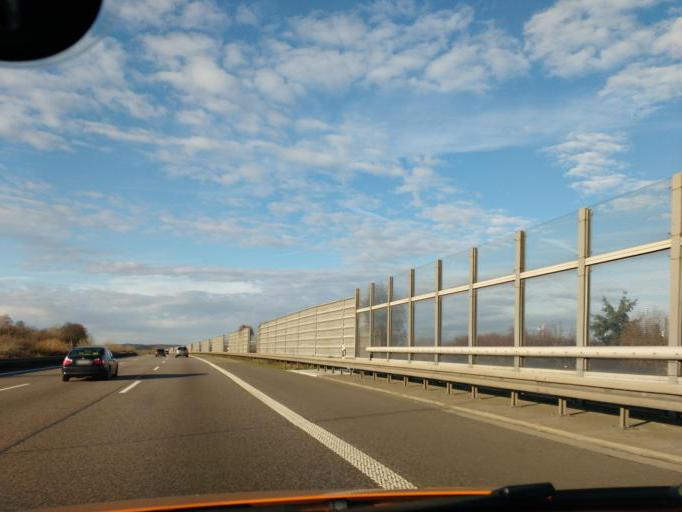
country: DE
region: Saxony-Anhalt
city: Wefensleben
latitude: 52.2076
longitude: 11.1673
